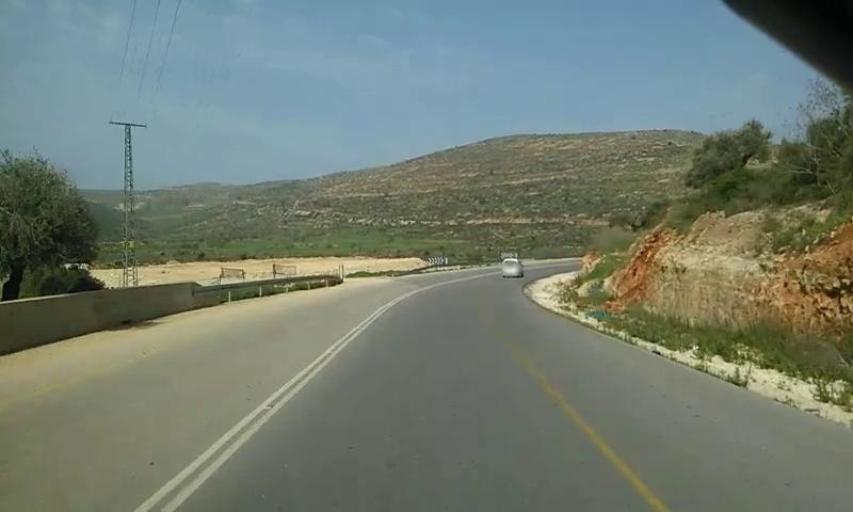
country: PS
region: West Bank
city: `Atarah
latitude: 31.9865
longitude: 35.2282
